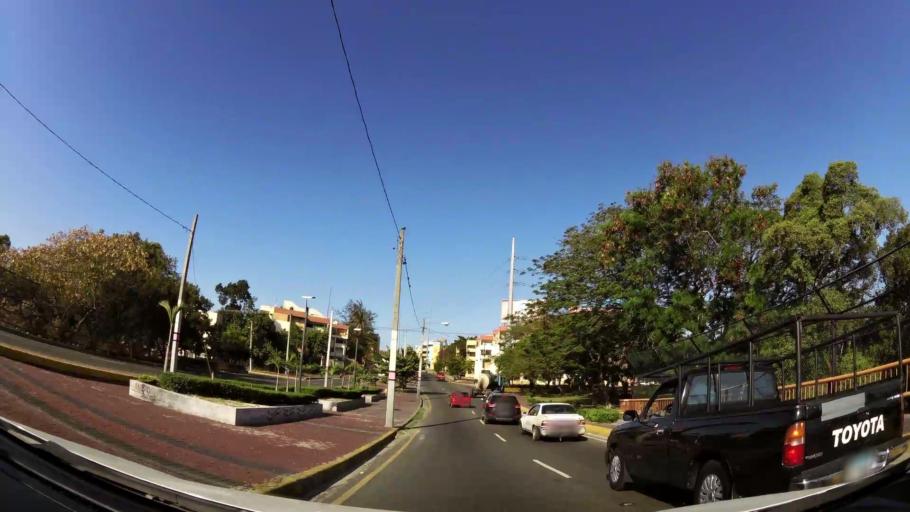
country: DO
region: Nacional
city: San Carlos
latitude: 18.4812
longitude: -69.8844
